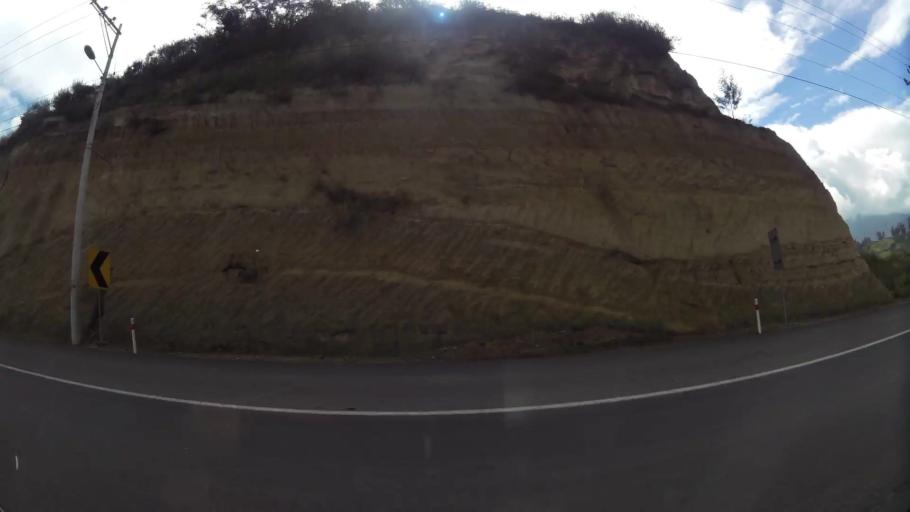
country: EC
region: Pichincha
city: Sangolqui
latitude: -0.3231
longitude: -78.4063
